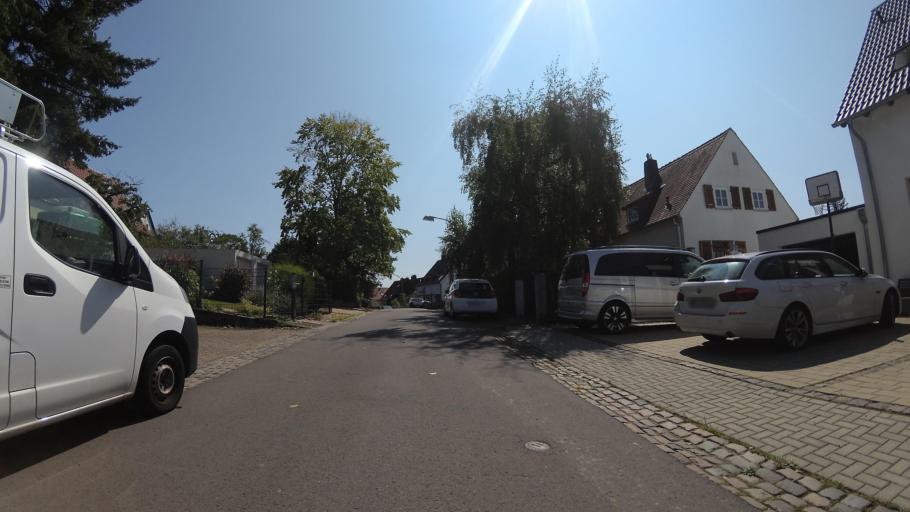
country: DE
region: Saarland
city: Saarbrucken
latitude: 49.2220
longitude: 6.9768
